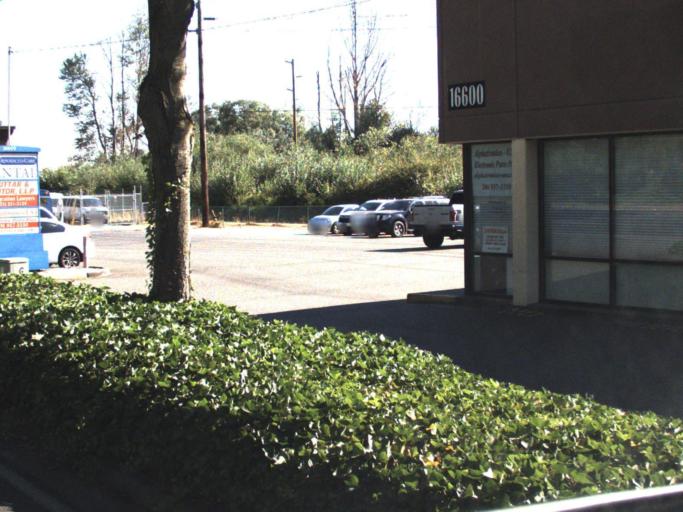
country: US
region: Washington
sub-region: King County
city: Tukwila
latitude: 47.4541
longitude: -122.2432
